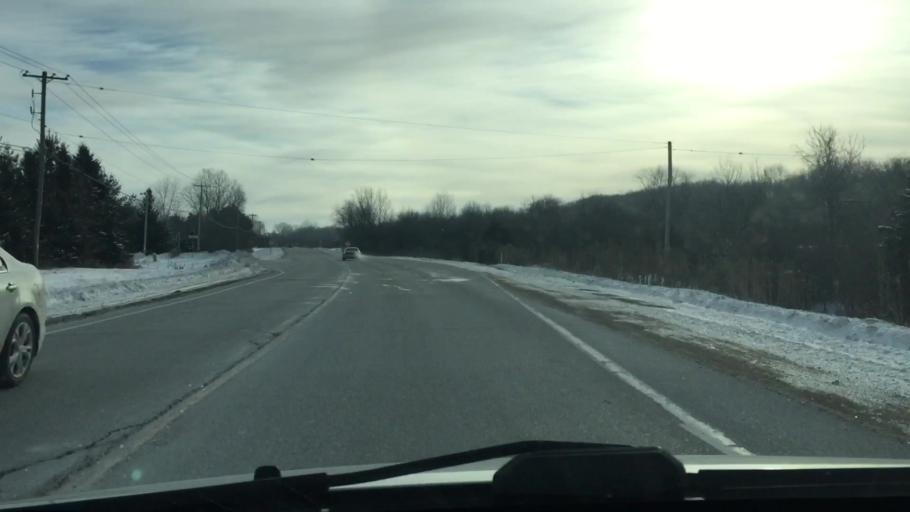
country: US
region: Wisconsin
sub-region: Waukesha County
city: Wales
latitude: 43.0128
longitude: -88.3987
